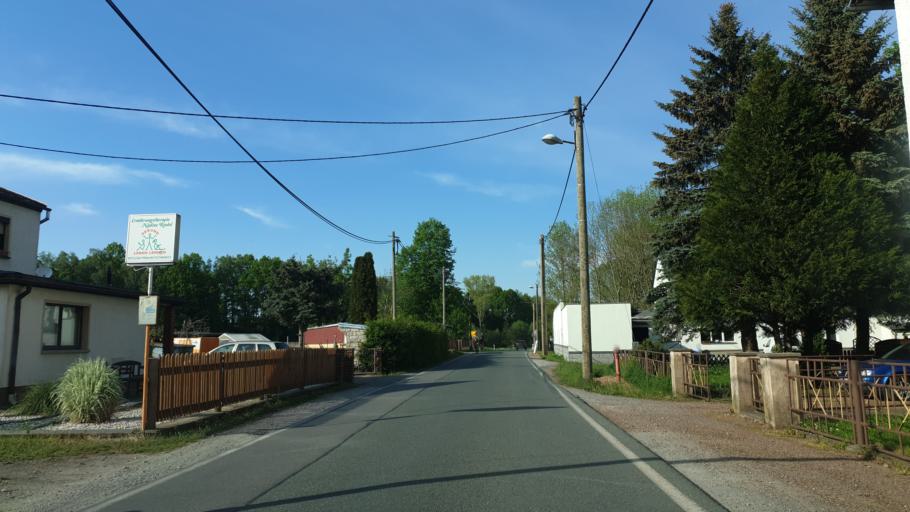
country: DE
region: Saxony
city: Neukirchen
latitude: 50.7630
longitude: 12.8637
